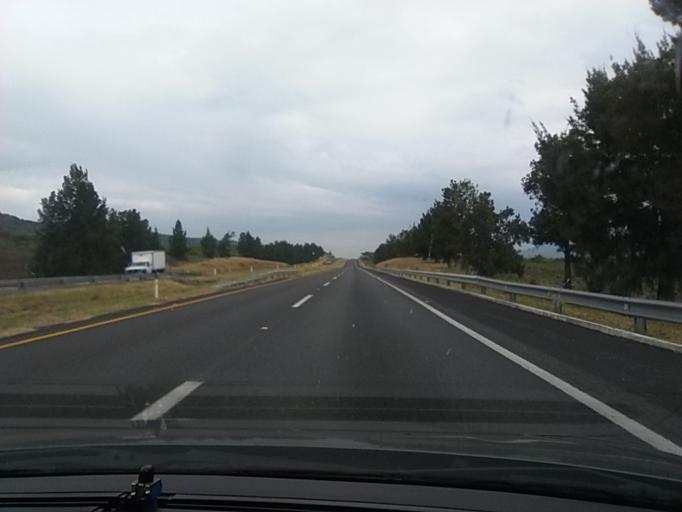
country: MX
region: Michoacan
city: Churintzio
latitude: 20.1168
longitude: -102.0487
